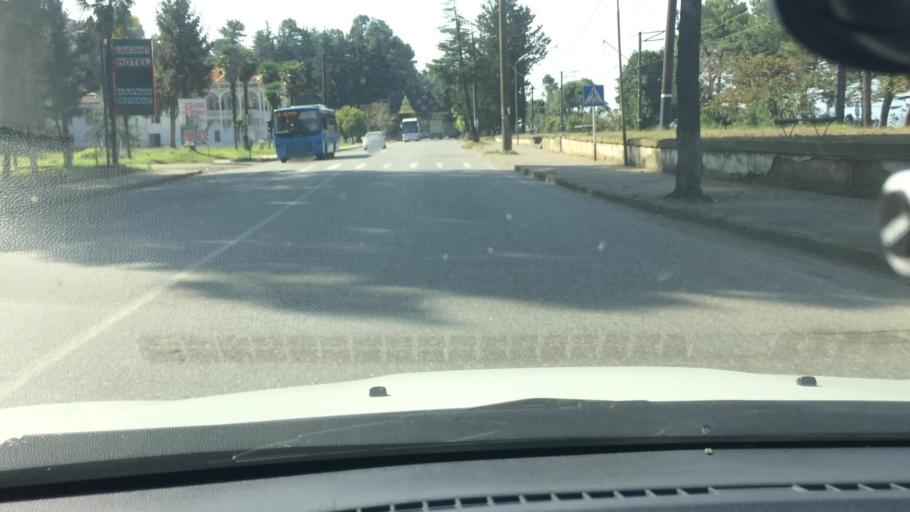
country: GE
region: Ajaria
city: Makhinjauri
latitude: 41.6762
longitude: 41.6959
